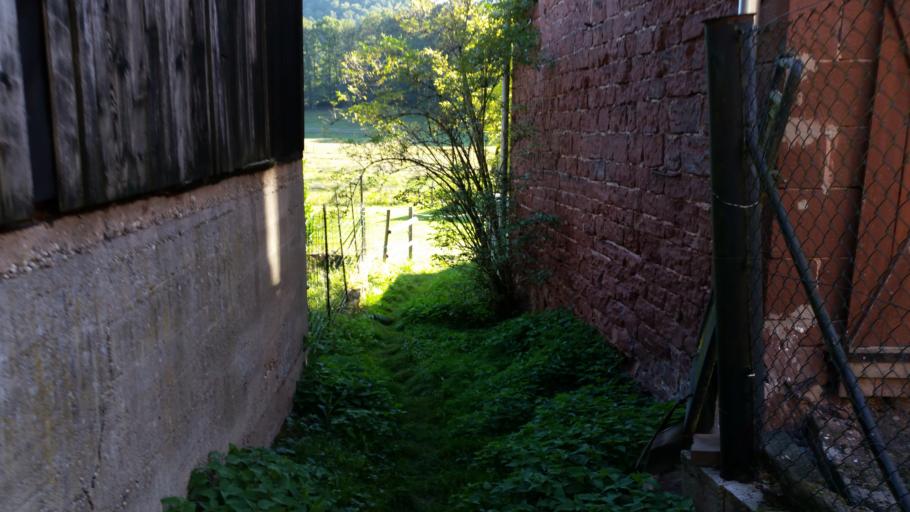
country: DE
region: Rheinland-Pfalz
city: Ludwigswinkel
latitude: 49.0365
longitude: 7.6839
